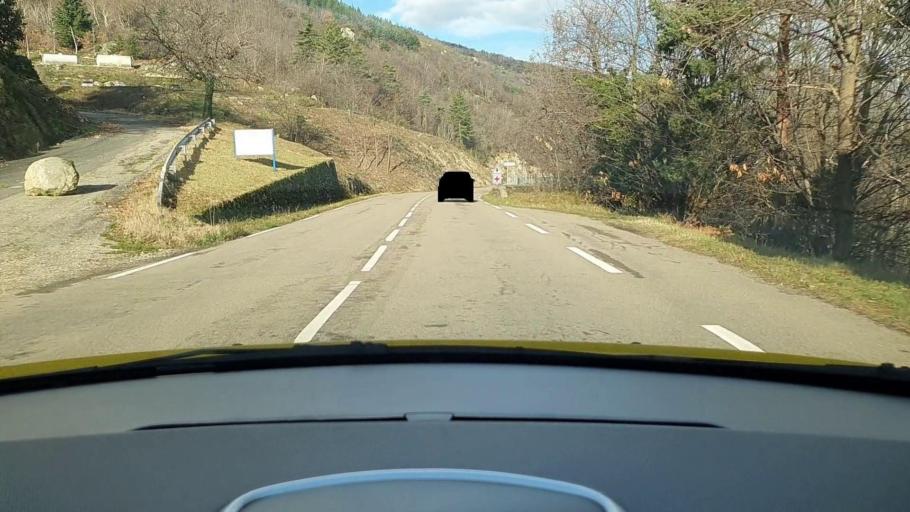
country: FR
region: Languedoc-Roussillon
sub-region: Departement du Gard
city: Branoux-les-Taillades
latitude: 44.3963
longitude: 3.9349
